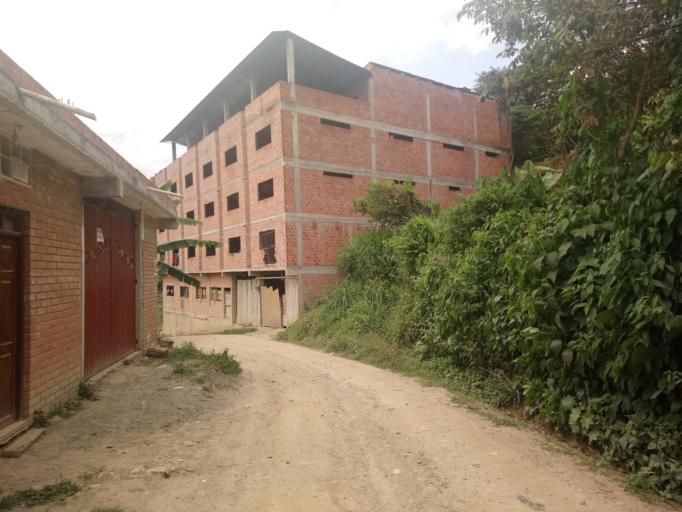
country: BO
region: La Paz
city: Coroico
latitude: -16.1883
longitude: -67.7294
